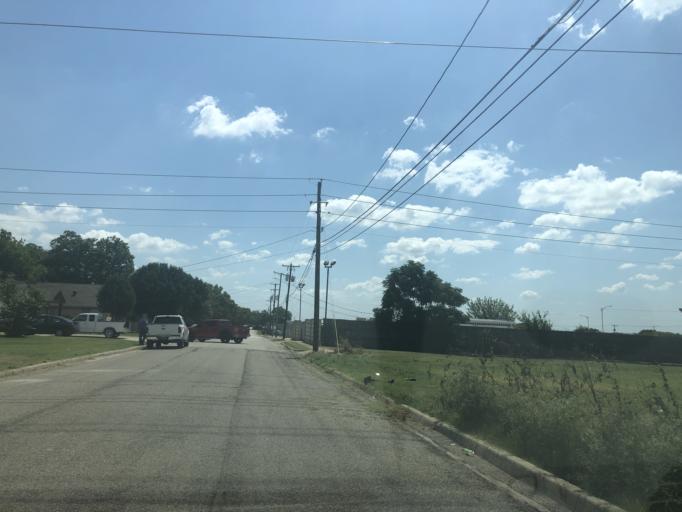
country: US
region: Texas
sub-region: Dallas County
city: Grand Prairie
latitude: 32.7407
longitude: -97.0345
